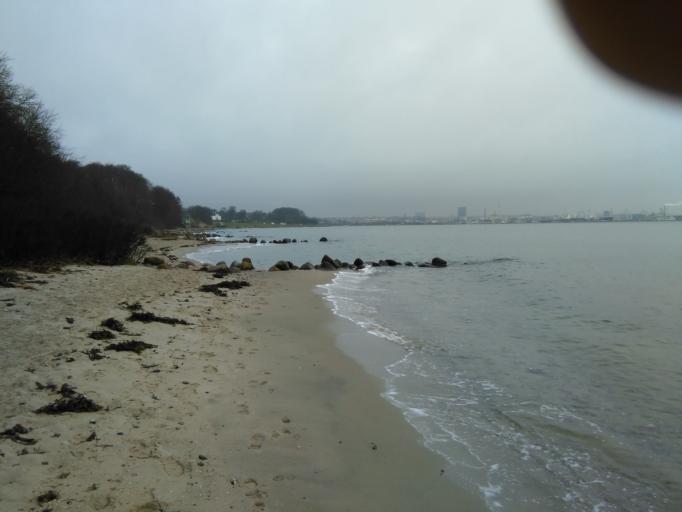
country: DK
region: Central Jutland
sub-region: Arhus Kommune
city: Arhus
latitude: 56.1232
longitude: 10.2207
